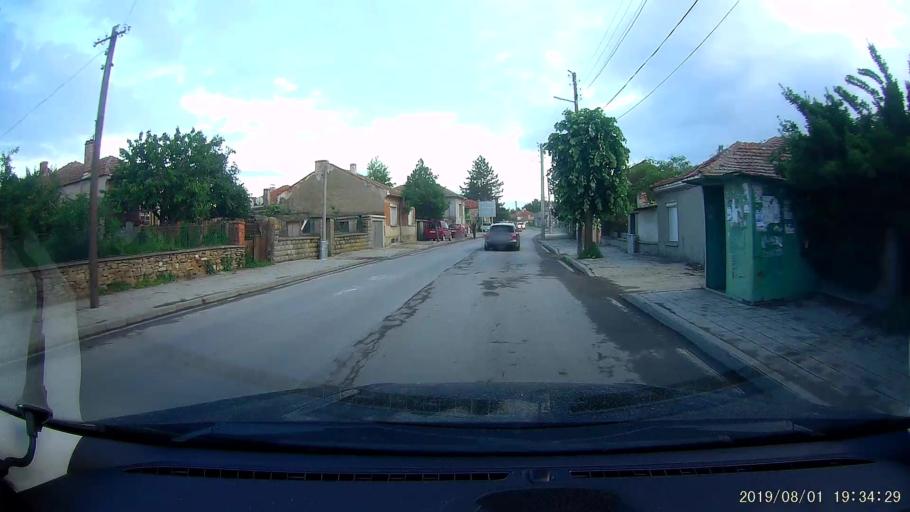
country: BG
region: Burgas
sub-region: Obshtina Sungurlare
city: Sungurlare
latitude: 42.7707
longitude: 26.8779
